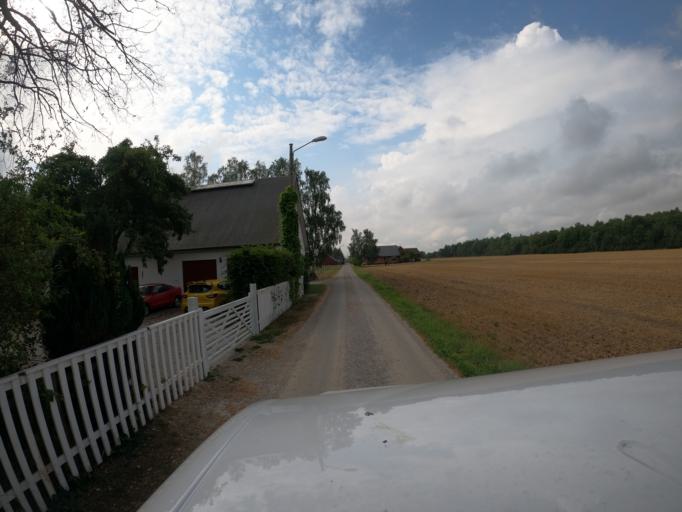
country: SE
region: Skane
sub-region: Lunds Kommun
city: Lund
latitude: 55.7277
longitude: 13.2961
